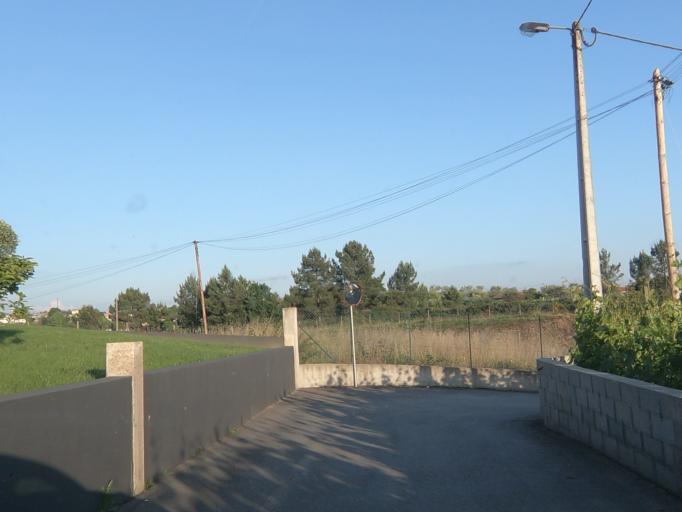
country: PT
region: Vila Real
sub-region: Vila Real
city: Vila Real
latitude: 41.2856
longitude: -7.7039
